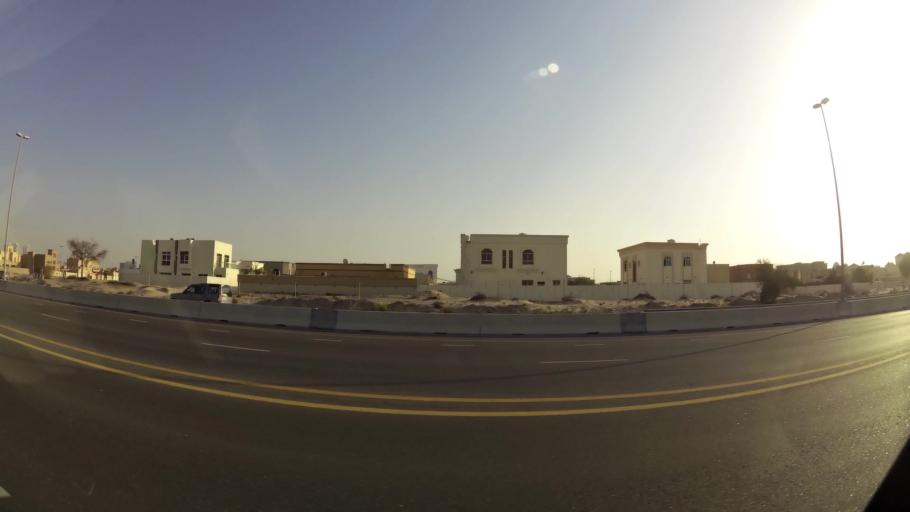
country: AE
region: Dubai
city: Dubai
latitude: 25.0972
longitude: 55.2400
